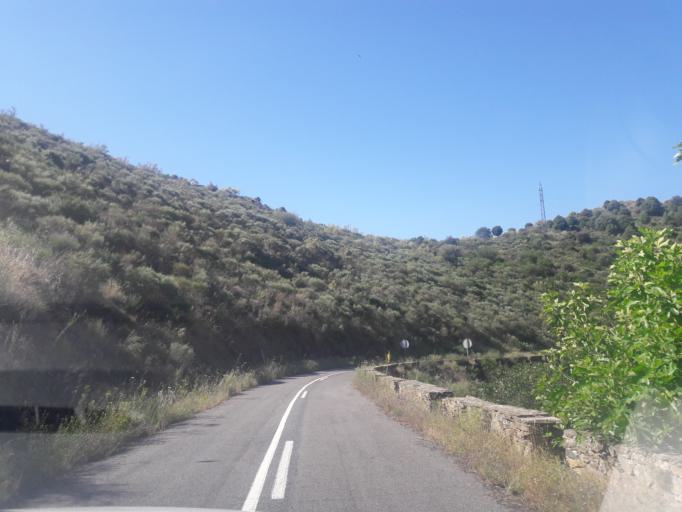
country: ES
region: Castille and Leon
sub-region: Provincia de Salamanca
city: Saucelle
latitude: 41.0321
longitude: -6.7414
